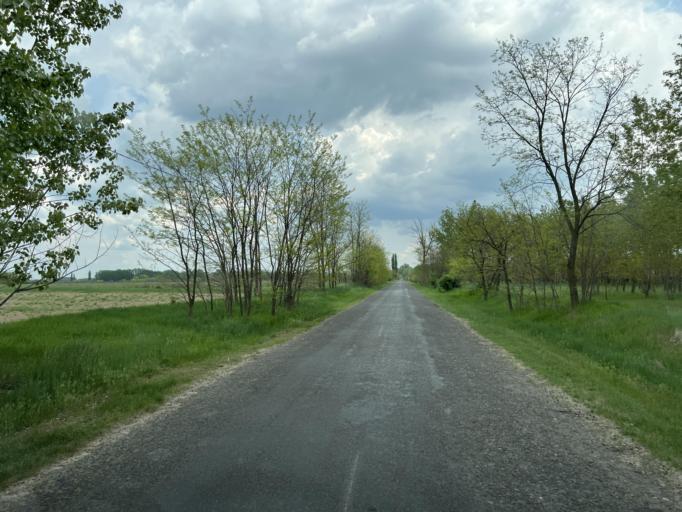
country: HU
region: Pest
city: Nagykoros
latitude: 47.0915
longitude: 19.7646
